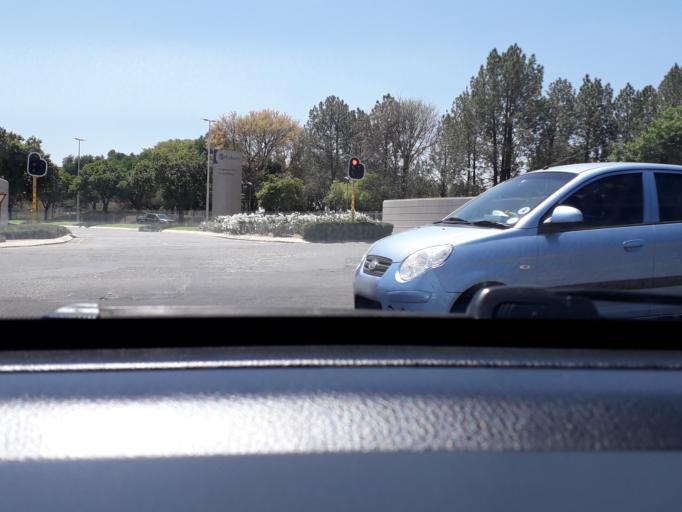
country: ZA
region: Gauteng
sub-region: City of Johannesburg Metropolitan Municipality
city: Midrand
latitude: -26.0416
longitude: 28.0859
